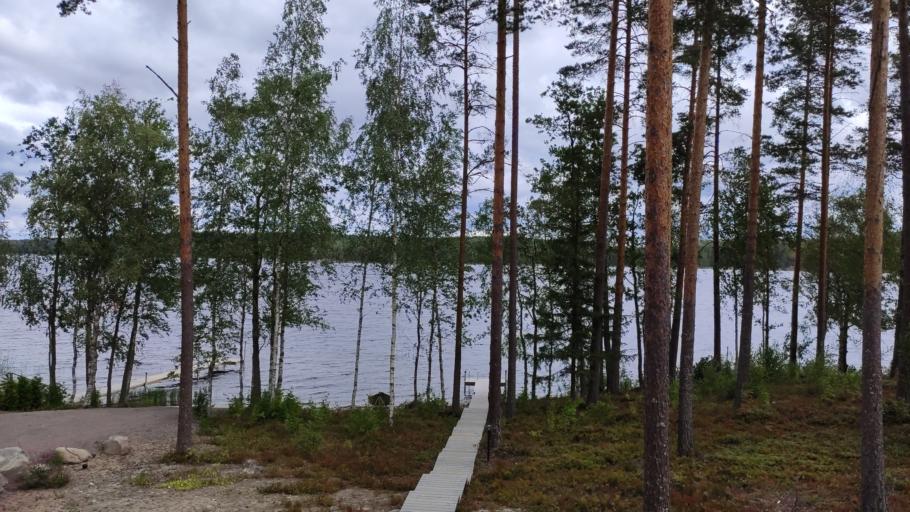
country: FI
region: Southern Savonia
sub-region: Mikkeli
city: Puumala
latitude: 61.3666
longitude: 28.3377
